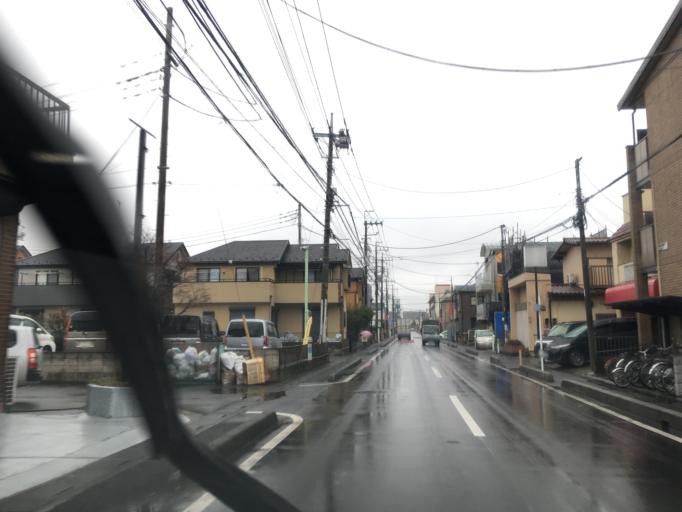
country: JP
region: Saitama
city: Koshigaya
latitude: 35.8881
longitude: 139.7789
